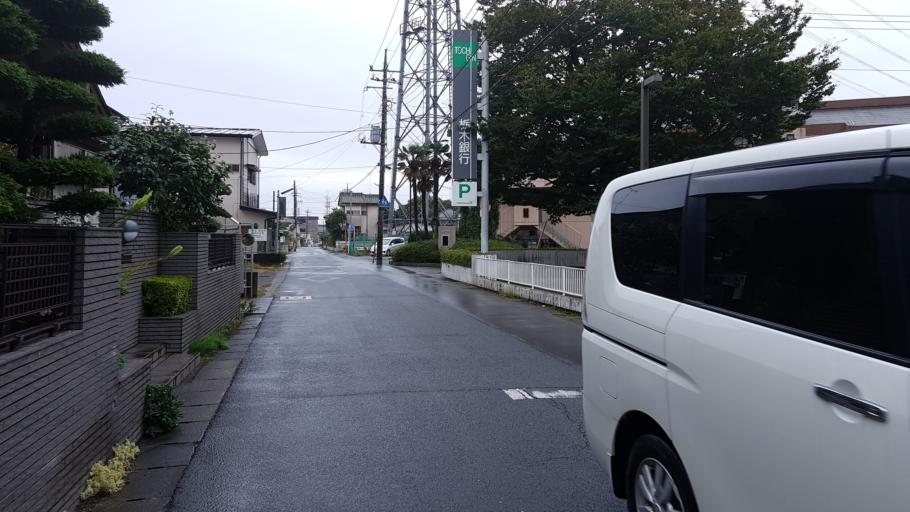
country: JP
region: Tochigi
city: Utsunomiya-shi
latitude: 36.5754
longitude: 139.9205
